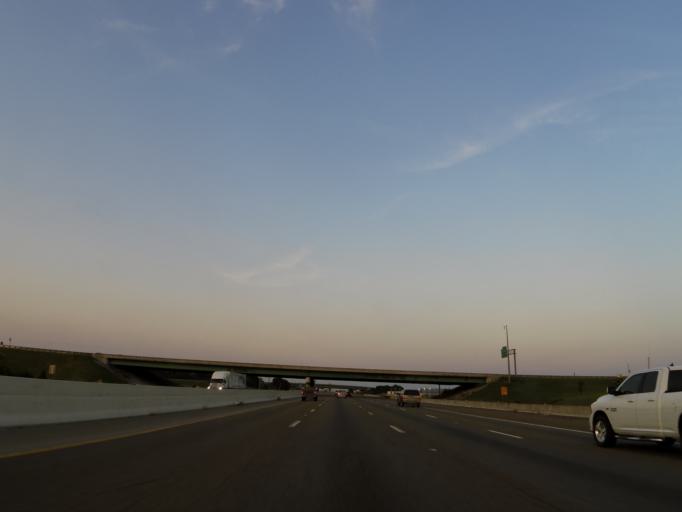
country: US
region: Tennessee
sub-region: Knox County
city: Farragut
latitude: 35.9108
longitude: -84.1236
